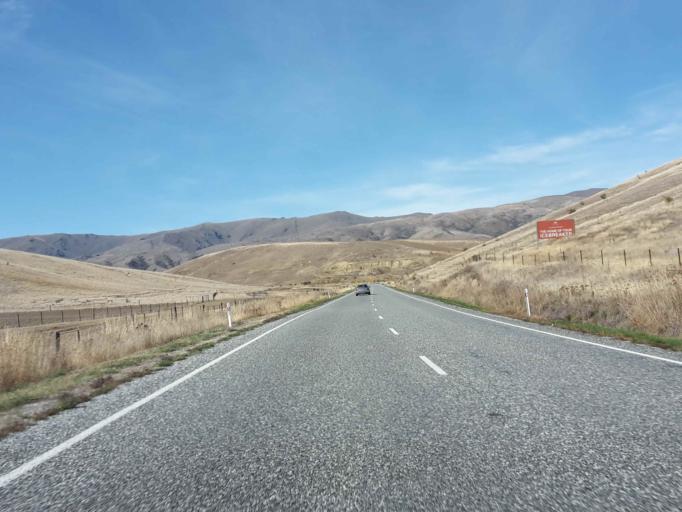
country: NZ
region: Otago
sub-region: Queenstown-Lakes District
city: Wanaka
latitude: -44.8063
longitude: 169.4848
